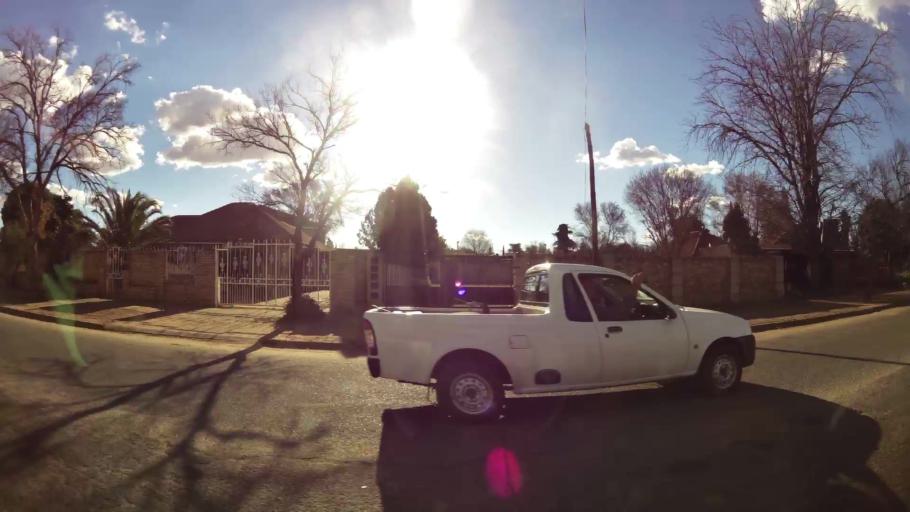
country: ZA
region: North-West
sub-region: Dr Kenneth Kaunda District Municipality
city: Klerksdorp
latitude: -26.8454
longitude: 26.6627
